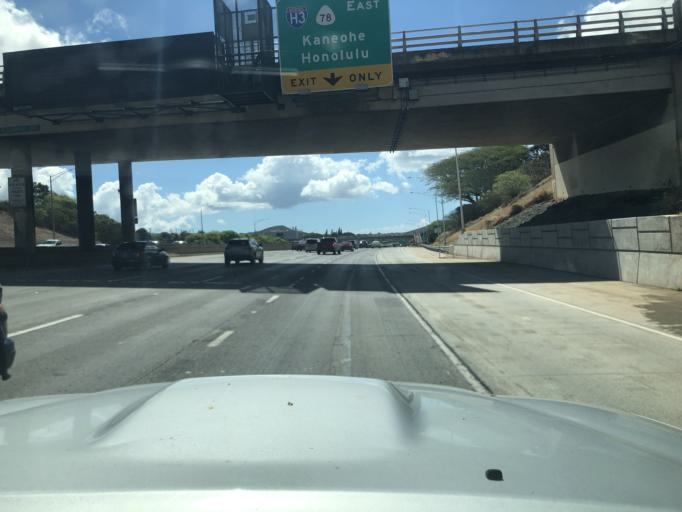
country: US
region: Hawaii
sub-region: Honolulu County
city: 'Aiea
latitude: 21.3846
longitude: -157.9329
